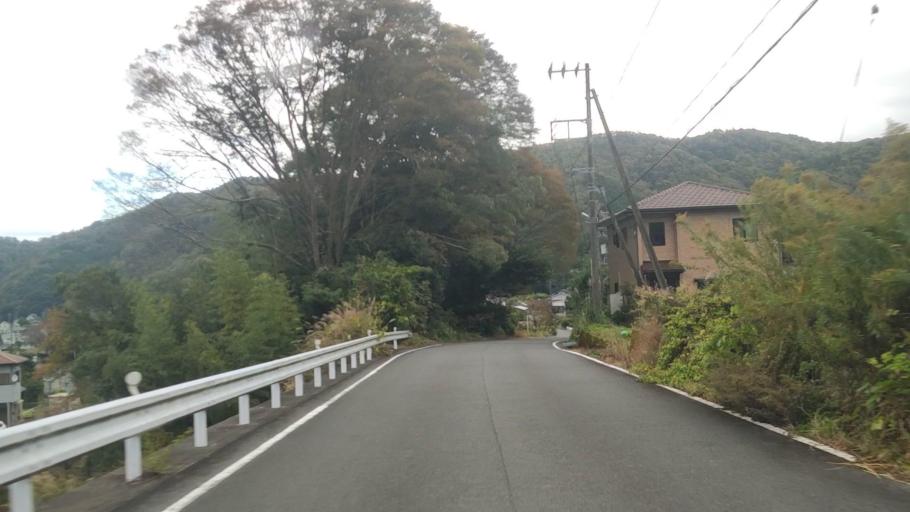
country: JP
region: Shizuoka
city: Ito
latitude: 34.9353
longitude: 138.9954
